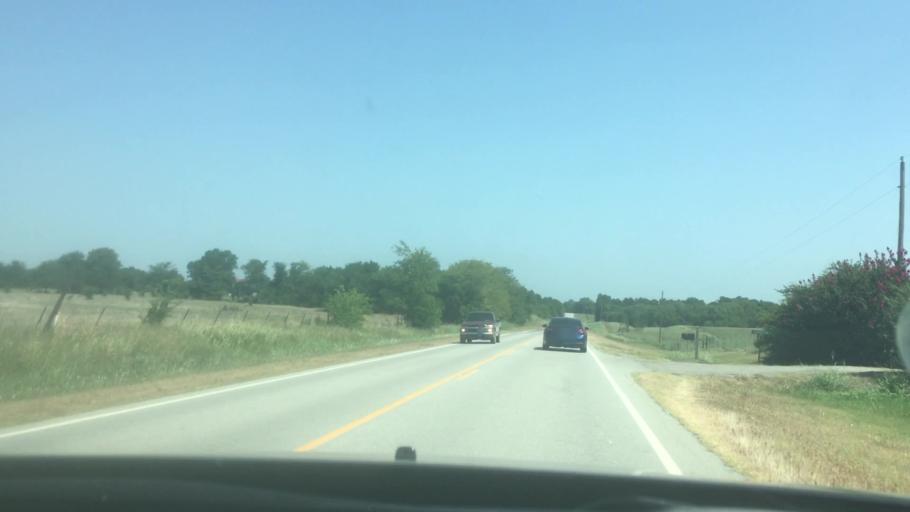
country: US
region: Oklahoma
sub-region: Coal County
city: Coalgate
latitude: 34.5215
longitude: -96.4070
